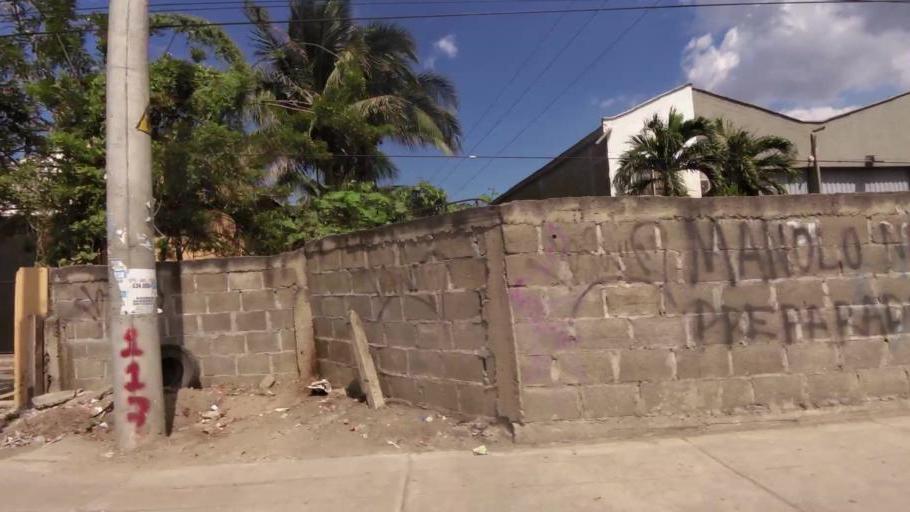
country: CO
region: Bolivar
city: Cartagena
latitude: 10.3784
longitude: -75.4621
